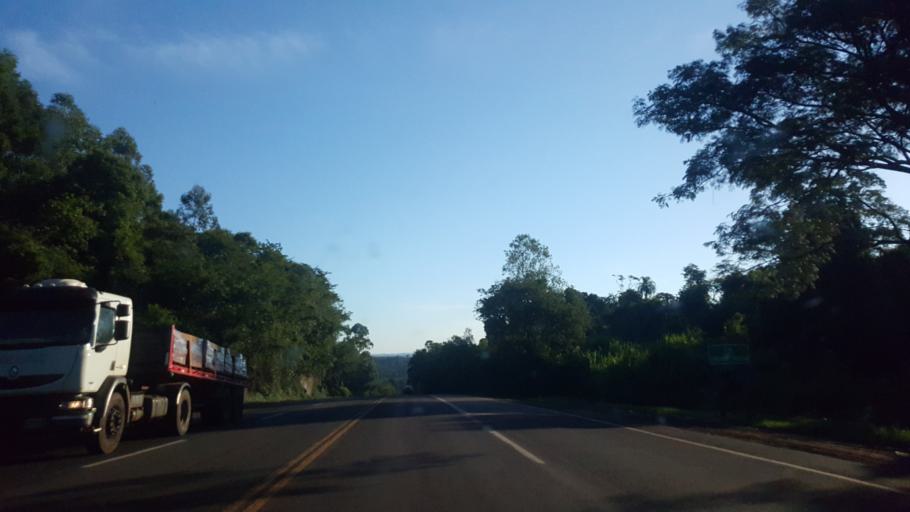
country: AR
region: Misiones
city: El Alcazar
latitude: -26.7265
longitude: -54.8678
